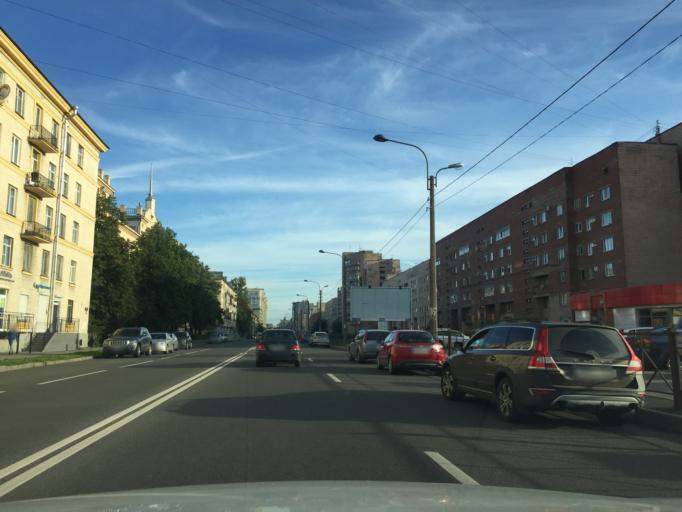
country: RU
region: St.-Petersburg
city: Kupchino
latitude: 59.8643
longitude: 30.3140
